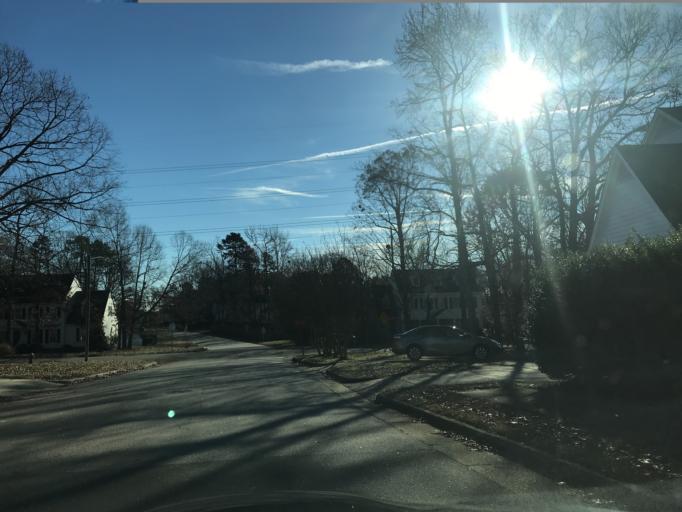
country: US
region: North Carolina
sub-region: Wake County
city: West Raleigh
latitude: 35.8964
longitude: -78.6034
